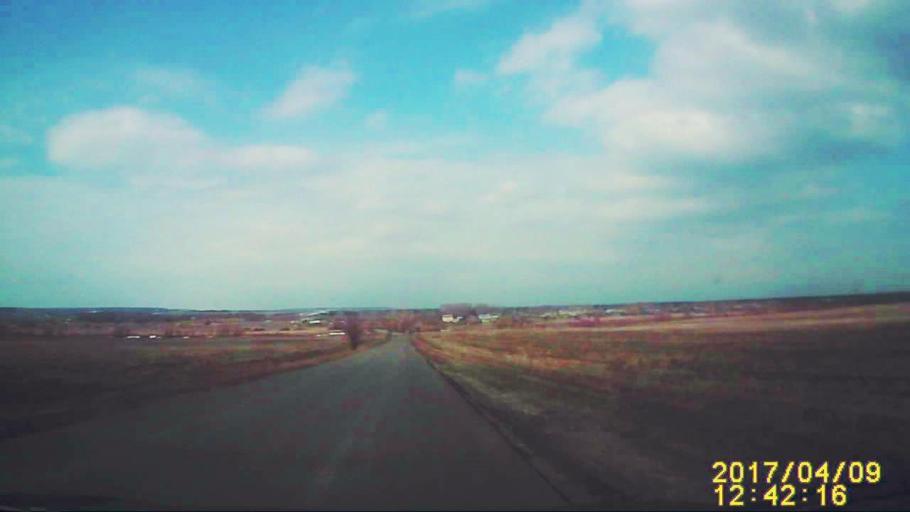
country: RU
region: Ulyanovsk
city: Ignatovka
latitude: 54.0021
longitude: 47.9290
